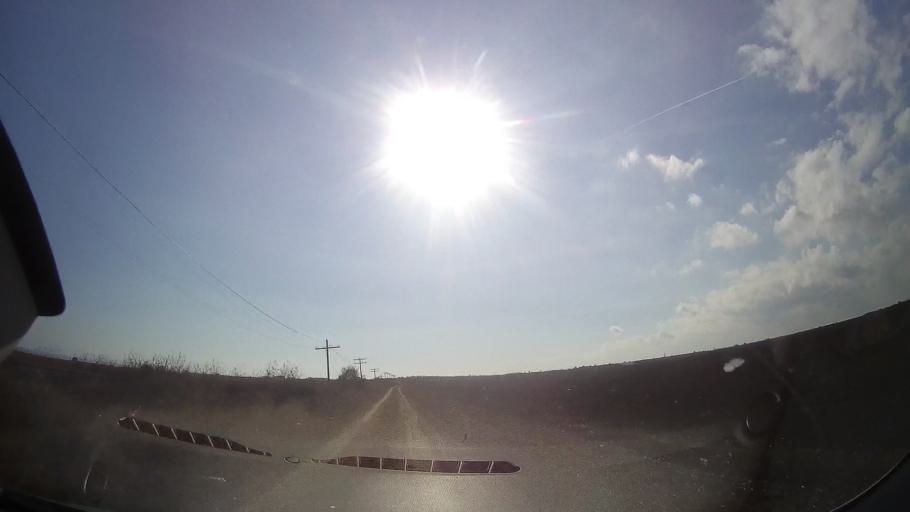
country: RO
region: Constanta
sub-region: Comuna Tuzla
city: Tuzla
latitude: 43.9823
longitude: 28.6445
